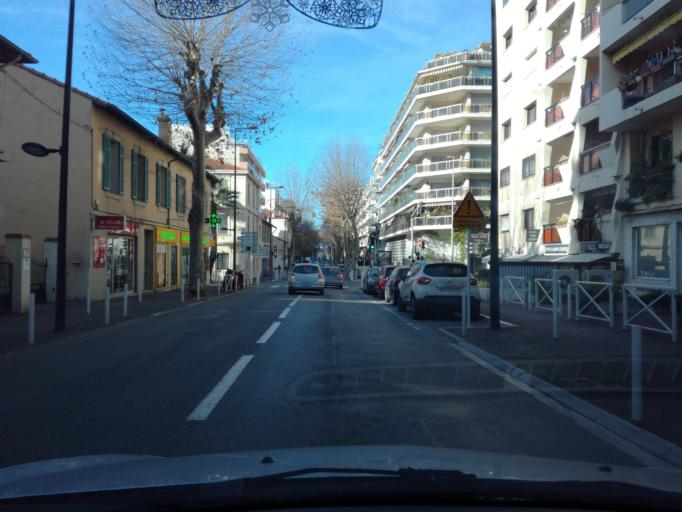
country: FR
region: Provence-Alpes-Cote d'Azur
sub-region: Departement des Alpes-Maritimes
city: Antibes
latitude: 43.5717
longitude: 7.1096
